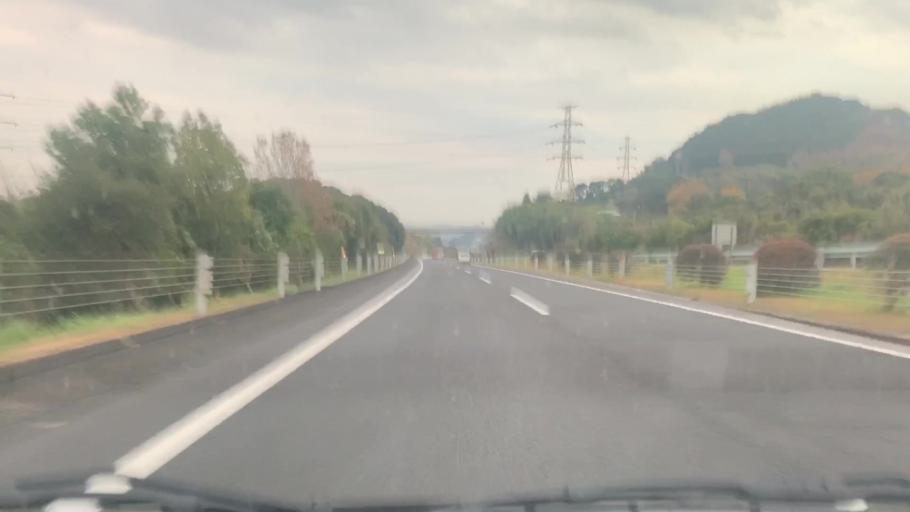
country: JP
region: Nagasaki
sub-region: Isahaya-shi
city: Isahaya
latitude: 32.8595
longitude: 130.0038
